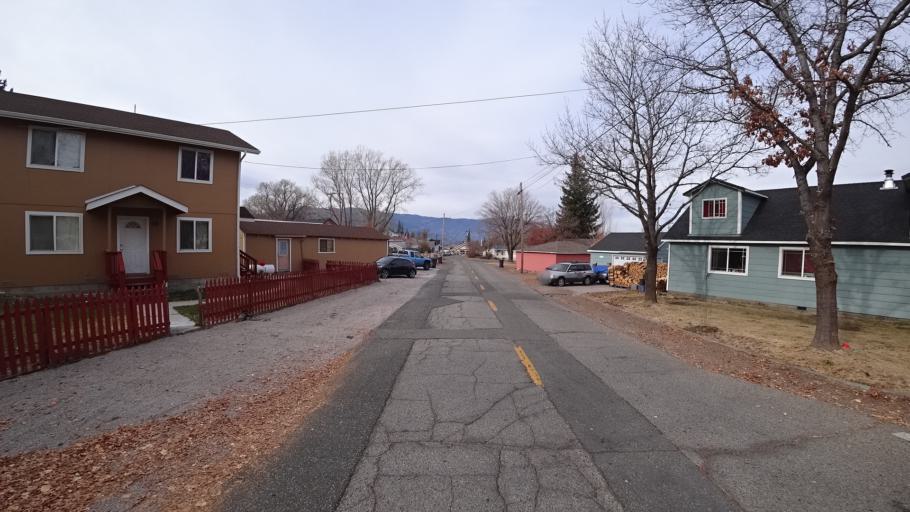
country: US
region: California
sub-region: Siskiyou County
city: Weed
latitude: 41.4310
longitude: -122.3753
